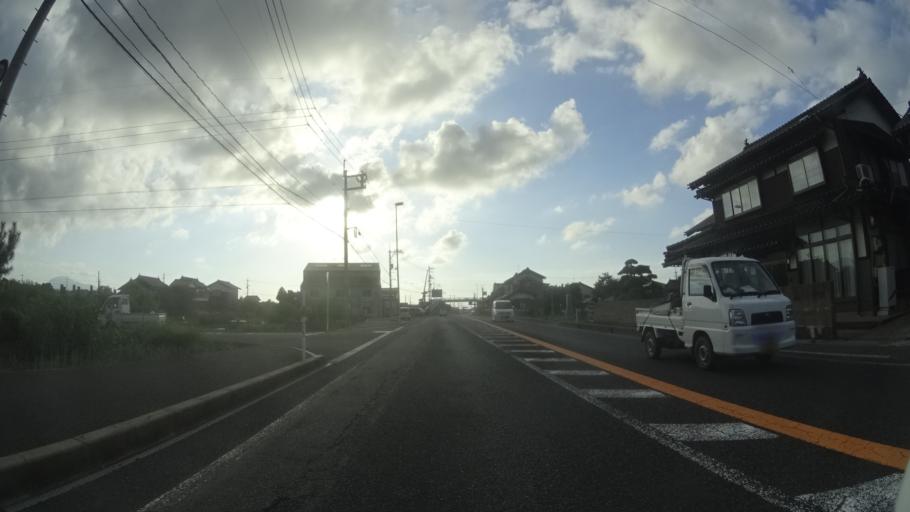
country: JP
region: Tottori
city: Kurayoshi
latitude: 35.5239
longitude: 133.5895
